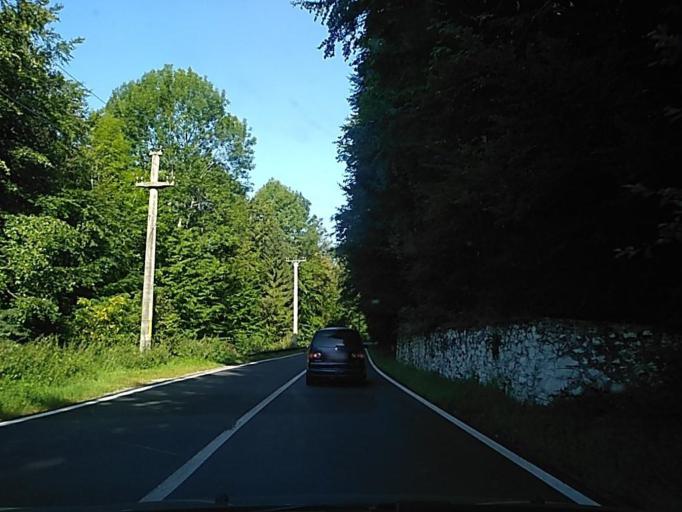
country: RO
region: Arges
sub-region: Comuna Arefu
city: Arefu
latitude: 45.3753
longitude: 24.6368
